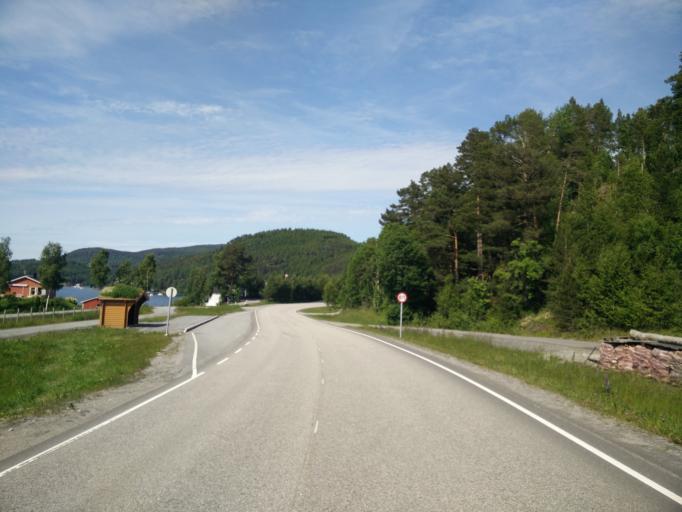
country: NO
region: More og Romsdal
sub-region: Kristiansund
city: Rensvik
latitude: 63.0142
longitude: 8.0027
